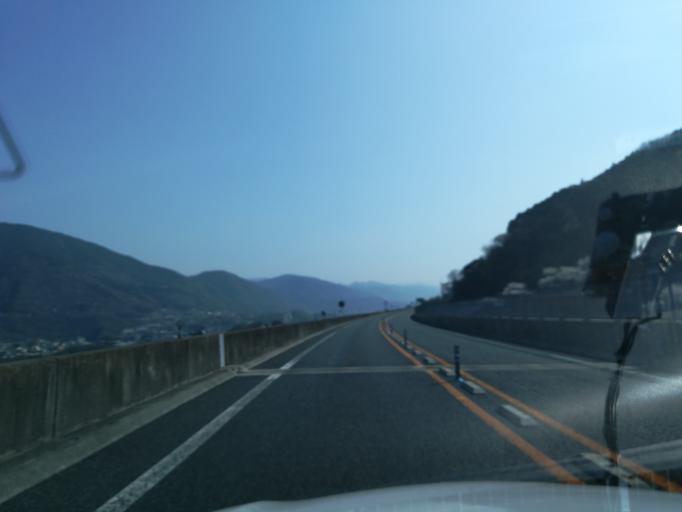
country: JP
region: Tokushima
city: Ikedacho
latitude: 34.0278
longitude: 133.8287
